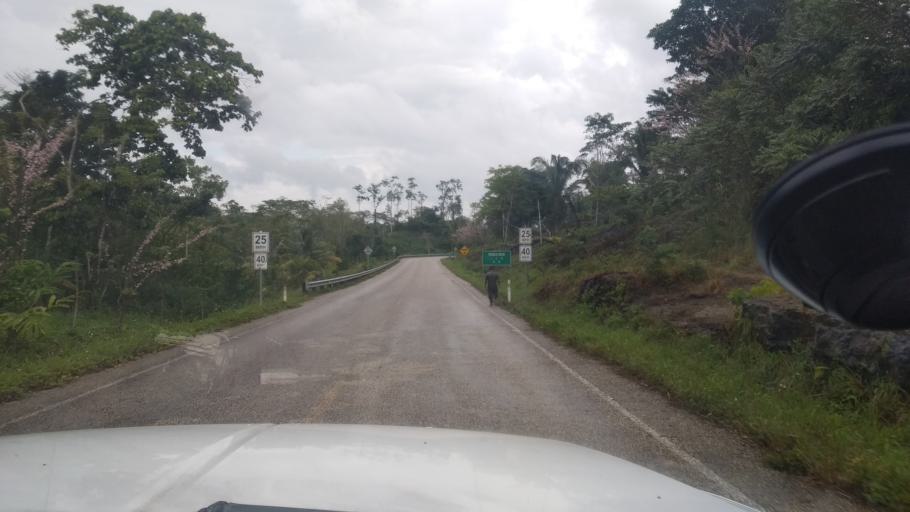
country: GT
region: Peten
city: San Luis
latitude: 16.2009
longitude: -89.1477
